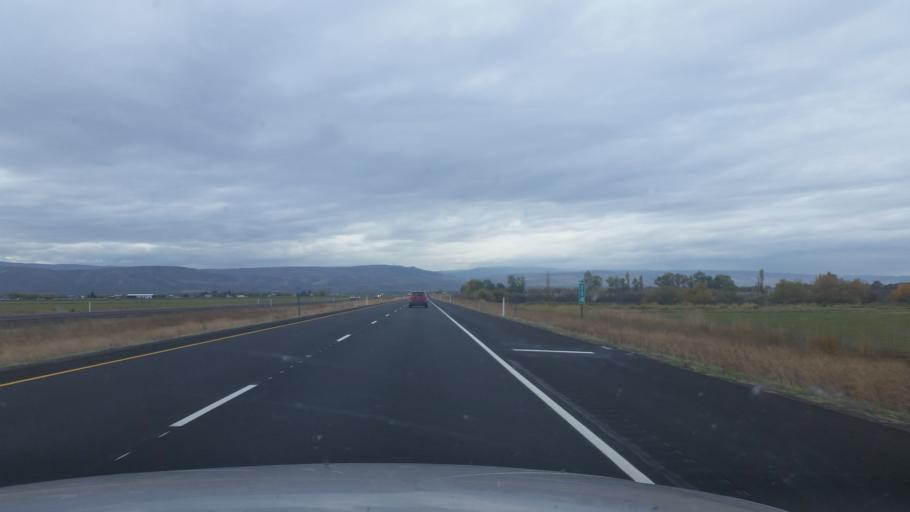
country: US
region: Washington
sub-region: Kittitas County
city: Kittitas
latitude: 46.9712
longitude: -120.4439
